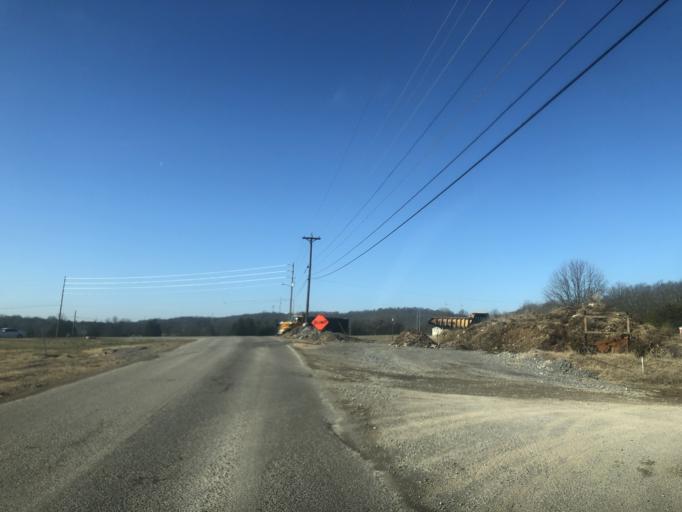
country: US
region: Tennessee
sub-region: Rutherford County
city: Smyrna
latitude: 35.9611
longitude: -86.5403
